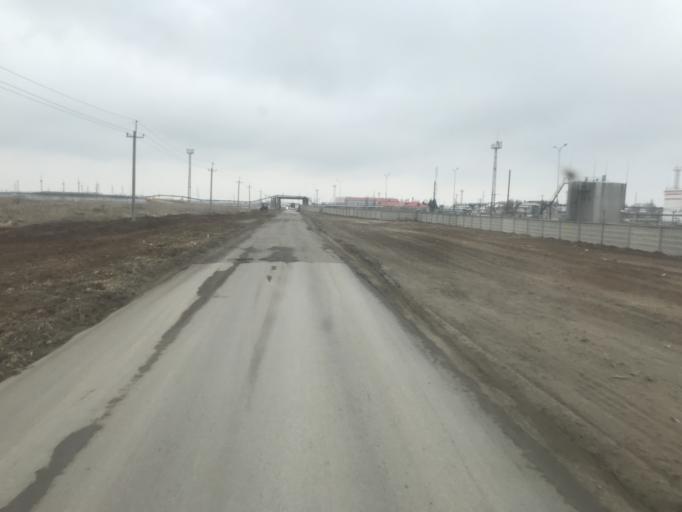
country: RU
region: Volgograd
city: Svetlyy Yar
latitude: 48.5067
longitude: 44.6432
